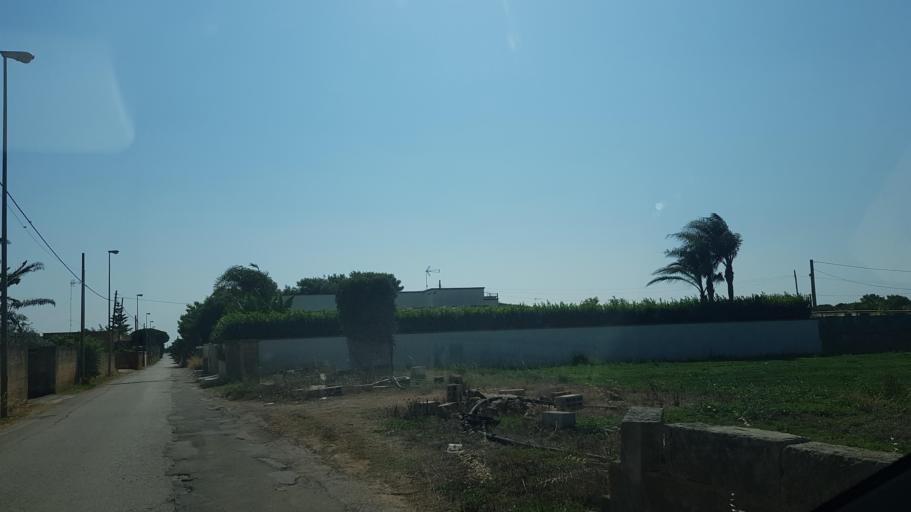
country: IT
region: Apulia
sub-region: Provincia di Lecce
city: Torre San Giovanni
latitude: 39.8905
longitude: 18.1262
